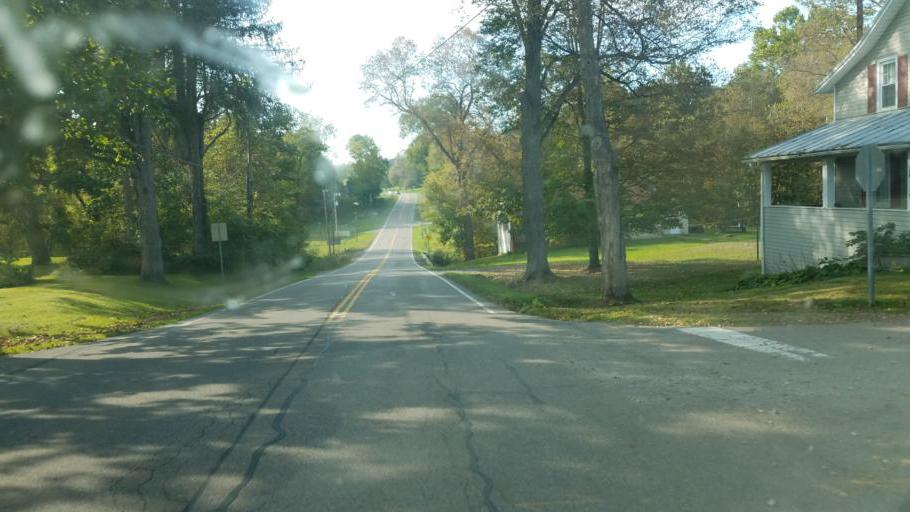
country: US
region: Ohio
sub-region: Knox County
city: Oak Hill
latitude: 40.3999
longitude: -82.2784
